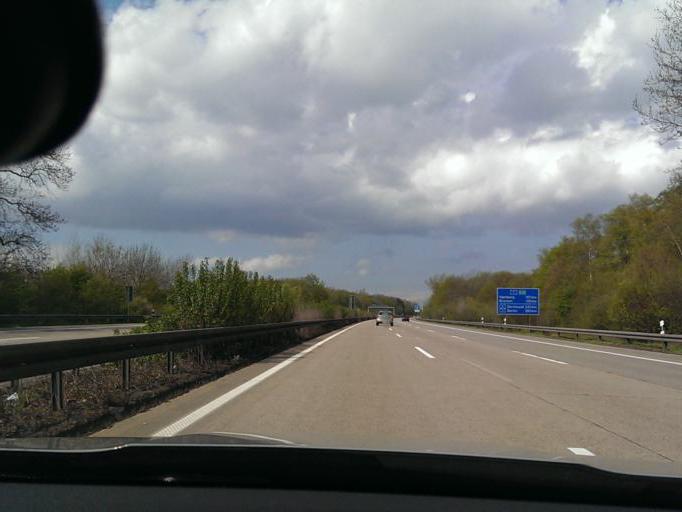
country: DE
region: Lower Saxony
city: Laatzen
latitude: 52.3147
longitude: 9.8673
